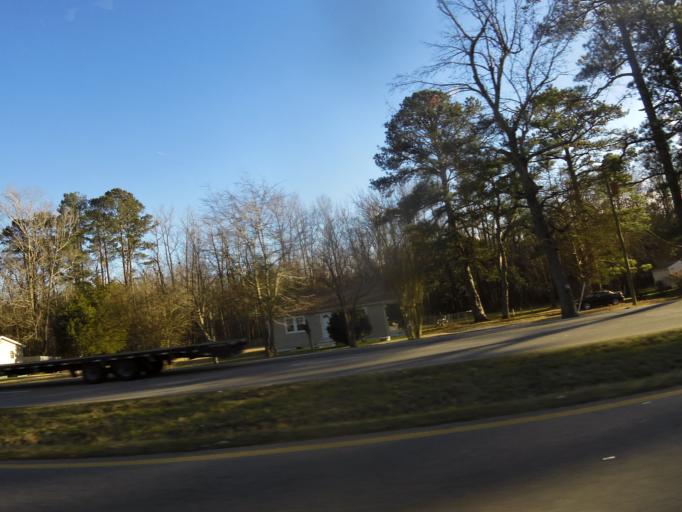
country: US
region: Virginia
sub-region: Isle of Wight County
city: Windsor
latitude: 36.6939
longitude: -76.7333
